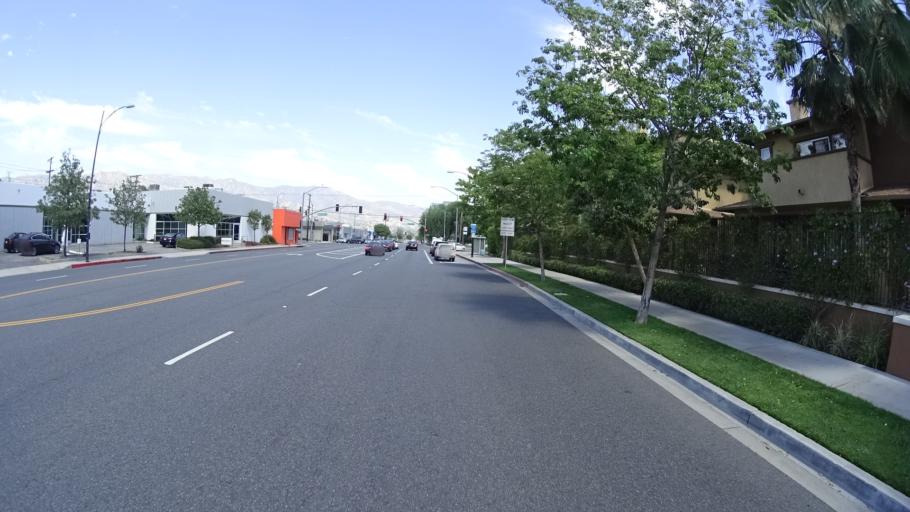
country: US
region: California
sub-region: Los Angeles County
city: Burbank
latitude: 34.1918
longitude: -118.3390
